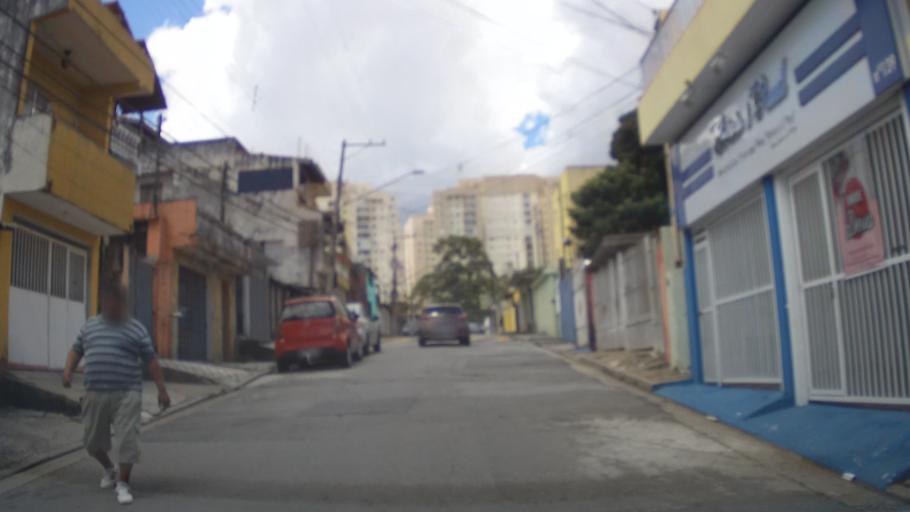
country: BR
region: Sao Paulo
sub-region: Guarulhos
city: Guarulhos
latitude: -23.4615
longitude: -46.5406
